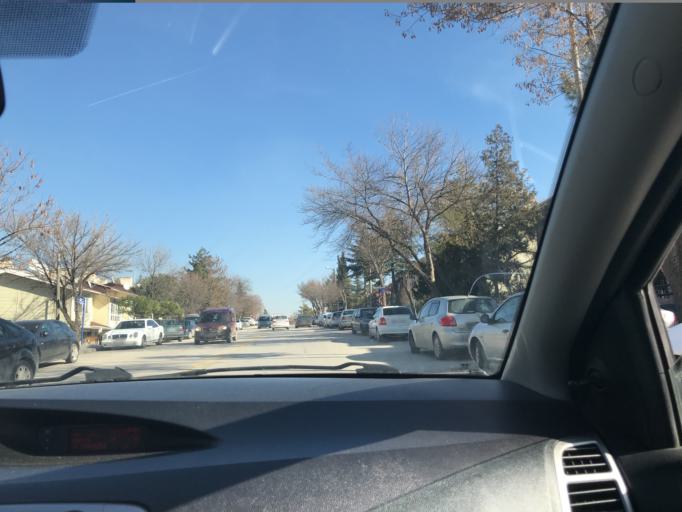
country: TR
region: Ankara
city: Batikent
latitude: 39.9711
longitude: 32.7292
